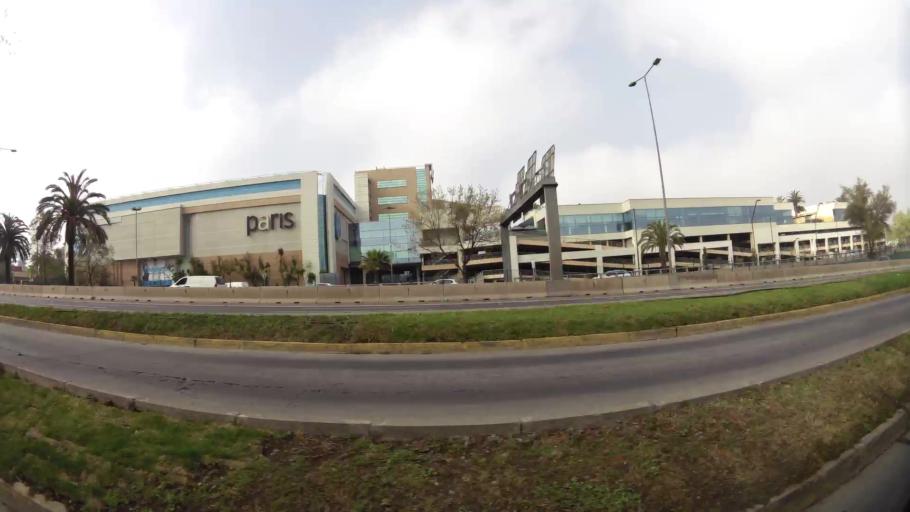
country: CL
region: Santiago Metropolitan
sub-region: Provincia de Santiago
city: Villa Presidente Frei, Nunoa, Santiago, Chile
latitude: -33.3889
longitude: -70.5466
